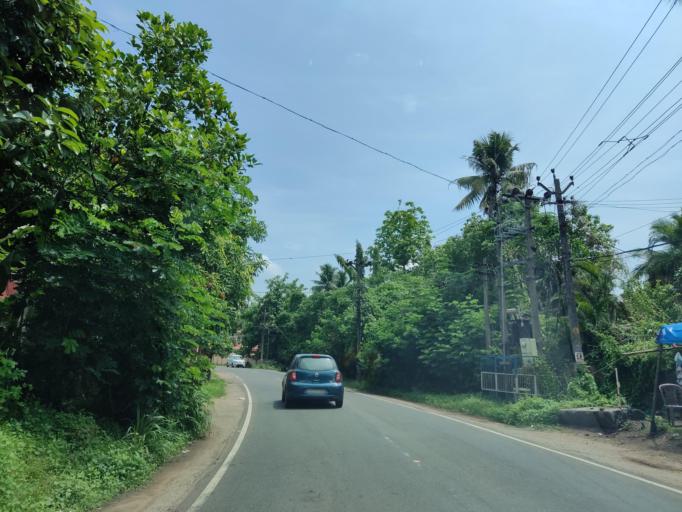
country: IN
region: Kerala
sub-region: Alappuzha
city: Chengannur
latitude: 9.3090
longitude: 76.5962
